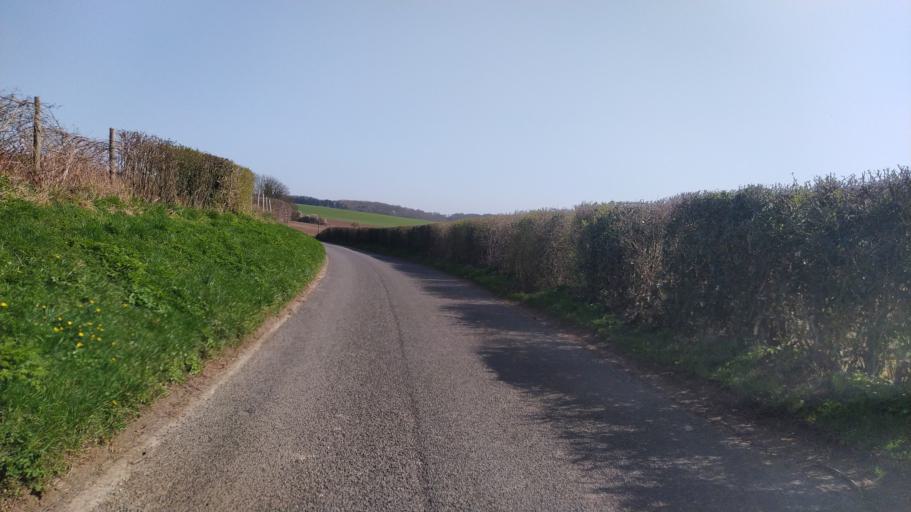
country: GB
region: England
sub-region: Hampshire
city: Kings Worthy
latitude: 51.0791
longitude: -1.2455
